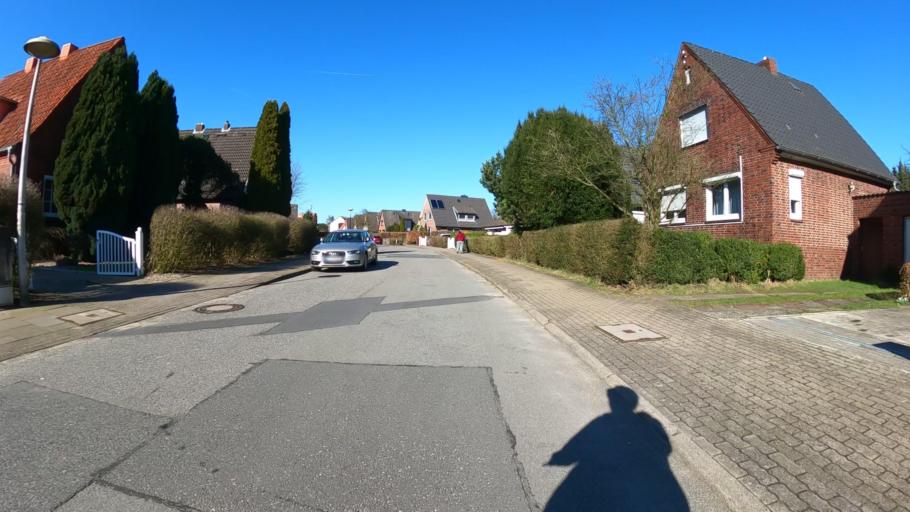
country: DE
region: Schleswig-Holstein
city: Pinneberg
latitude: 53.6650
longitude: 9.7879
